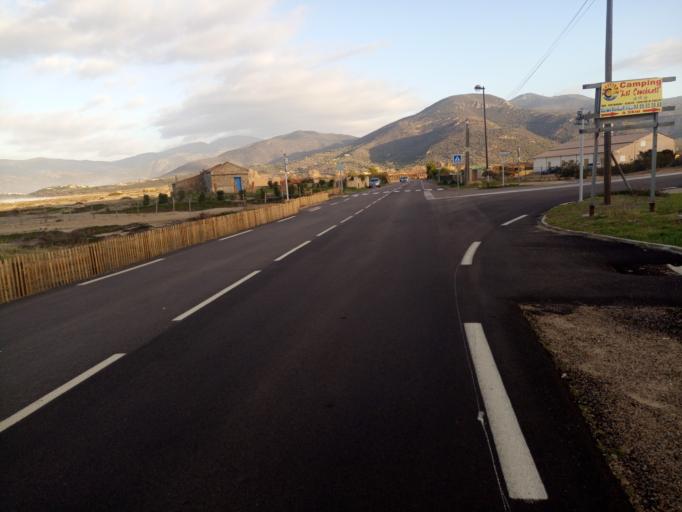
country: FR
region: Corsica
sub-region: Departement de la Corse-du-Sud
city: Appietto
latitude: 42.0699
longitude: 8.7223
